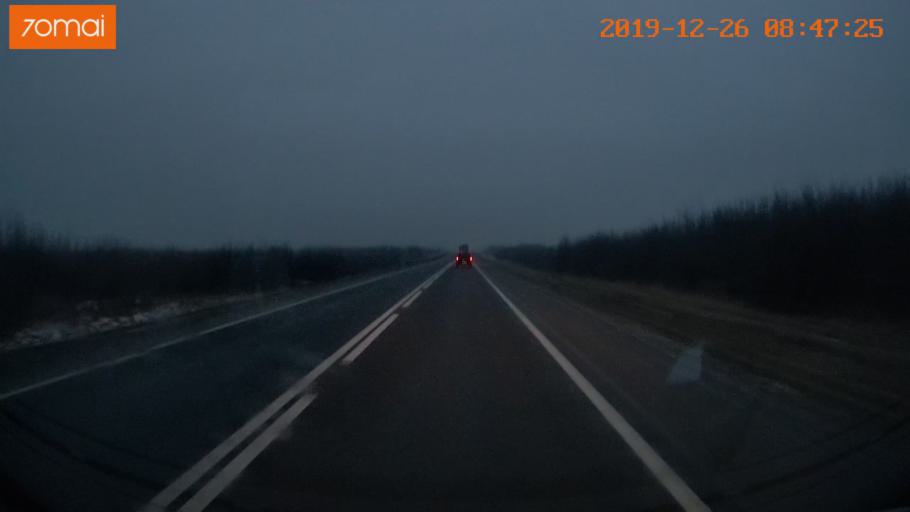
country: RU
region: Jaroslavl
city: Prechistoye
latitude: 58.6228
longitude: 40.3316
